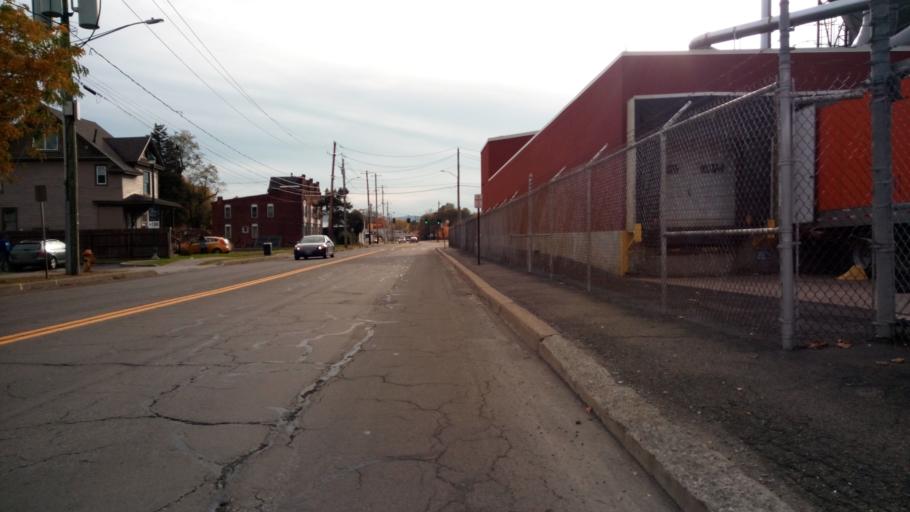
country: US
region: New York
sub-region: Chemung County
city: Elmira
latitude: 42.0855
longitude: -76.7989
